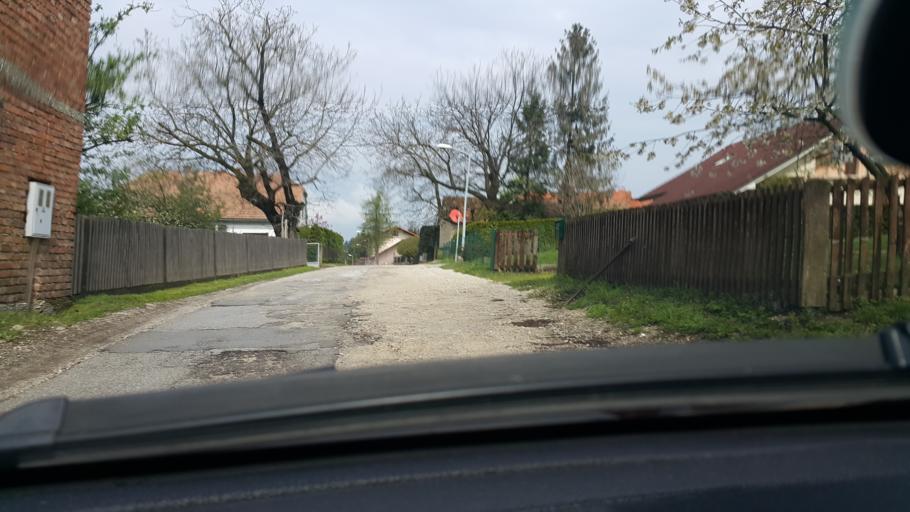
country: SI
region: Brezice
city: Brezice
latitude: 45.9033
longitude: 15.6513
